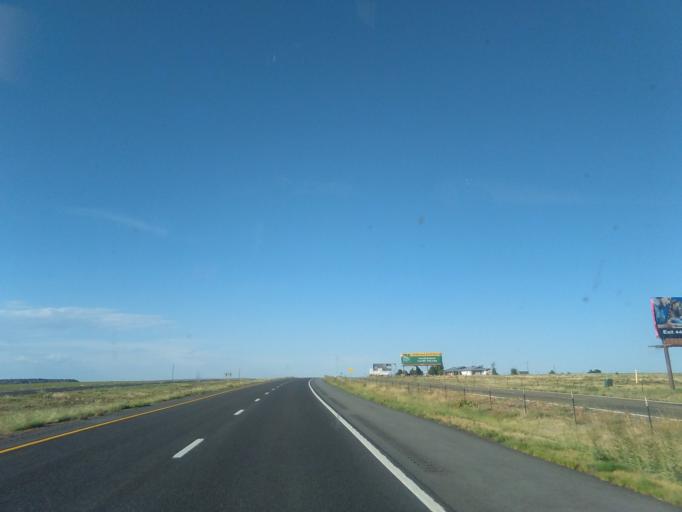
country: US
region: New Mexico
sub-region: San Miguel County
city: Las Vegas
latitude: 35.6685
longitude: -105.1822
